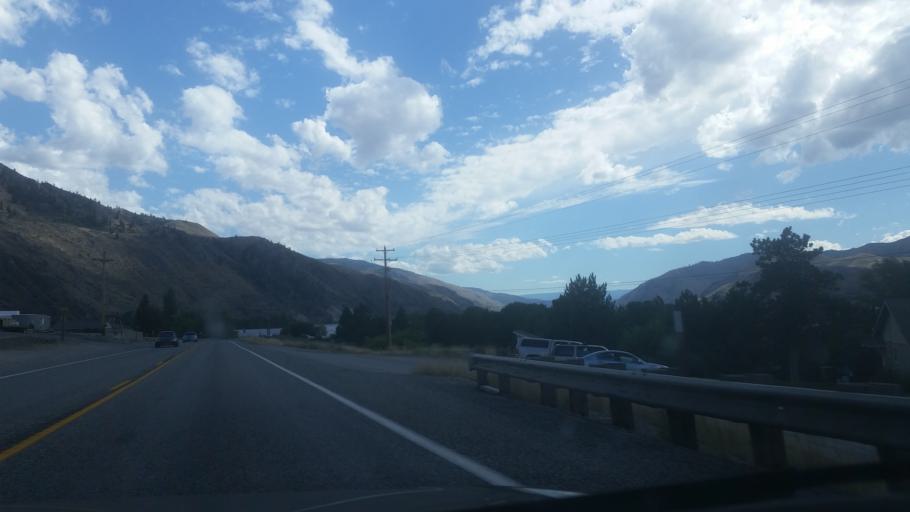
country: US
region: Washington
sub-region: Chelan County
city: Entiat
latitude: 47.7029
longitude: -120.1946
